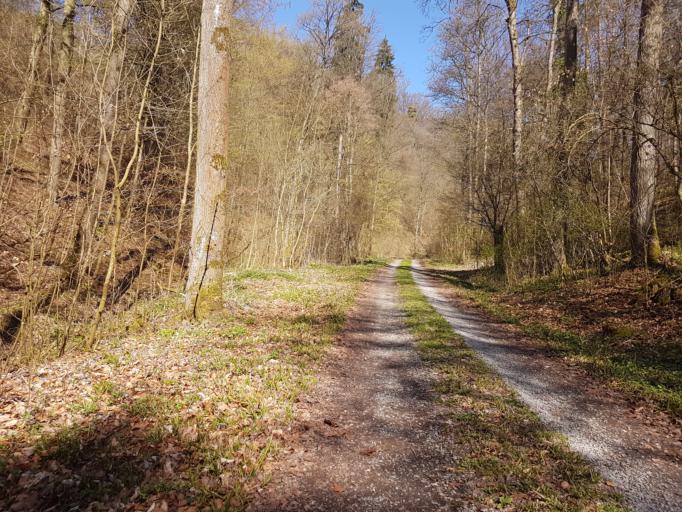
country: DE
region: Baden-Wuerttemberg
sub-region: Regierungsbezirk Stuttgart
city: Jagsthausen
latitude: 49.3332
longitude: 9.4888
